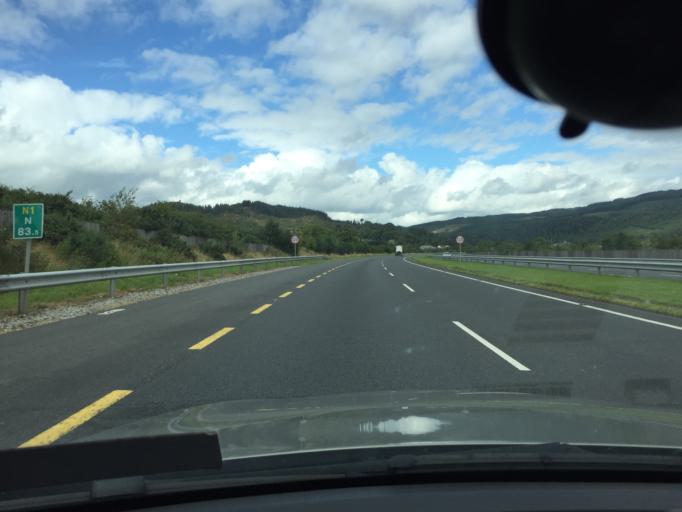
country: IE
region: Leinster
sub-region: Lu
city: Dundalk
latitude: 54.0556
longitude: -6.3583
